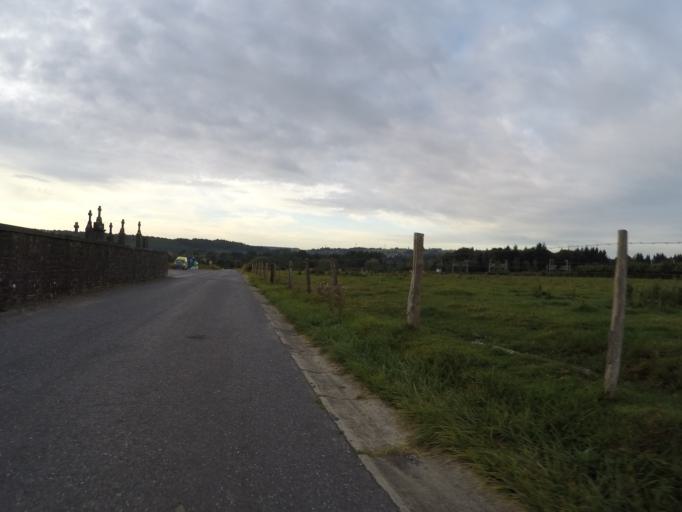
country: BE
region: Wallonia
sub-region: Province de Namur
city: Ciney
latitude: 50.3320
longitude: 5.0649
